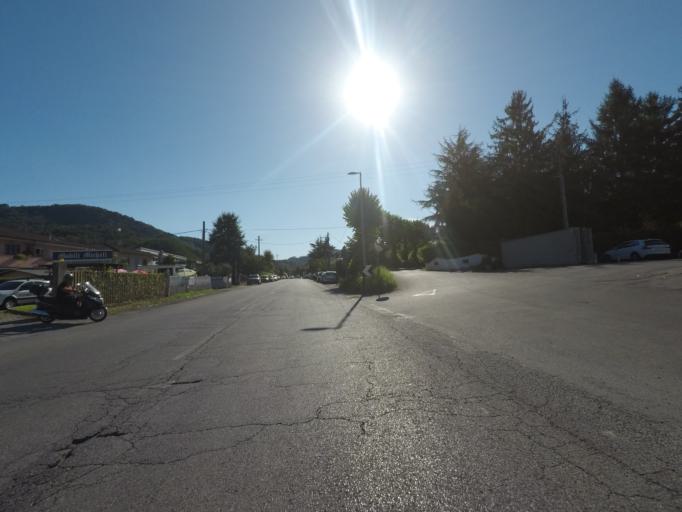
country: IT
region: Tuscany
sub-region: Provincia di Lucca
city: San Martino in Freddana-Monsagrati
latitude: 43.9051
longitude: 10.4167
